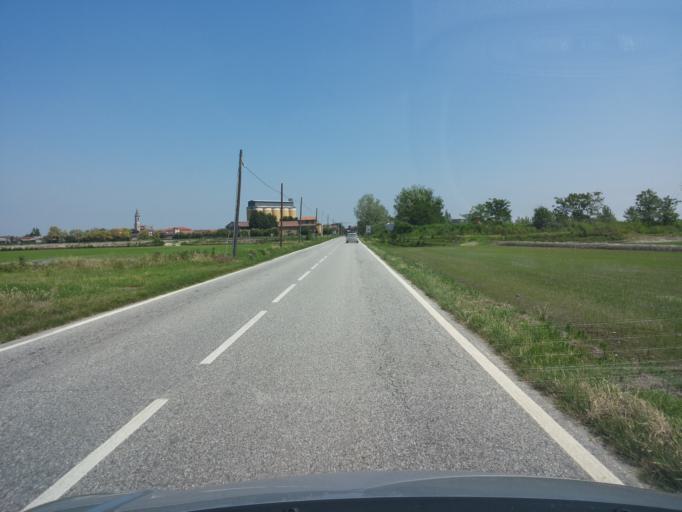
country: IT
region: Piedmont
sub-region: Provincia di Novara
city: Casalvolone
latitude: 45.3926
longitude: 8.4604
